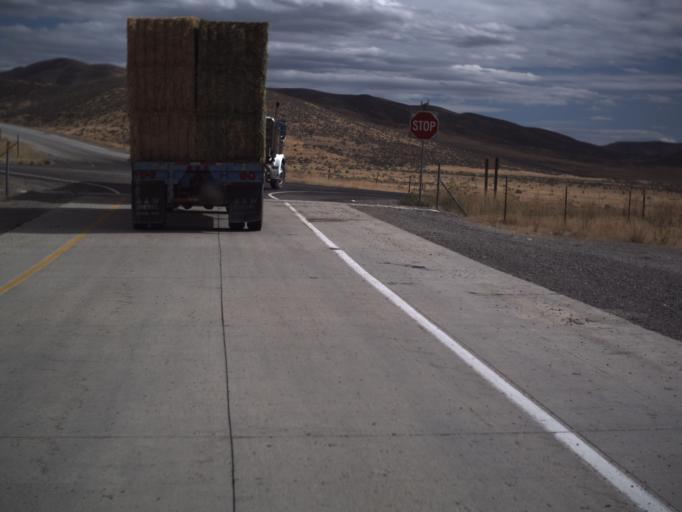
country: US
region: Utah
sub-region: Box Elder County
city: Garland
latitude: 41.8167
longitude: -112.4134
